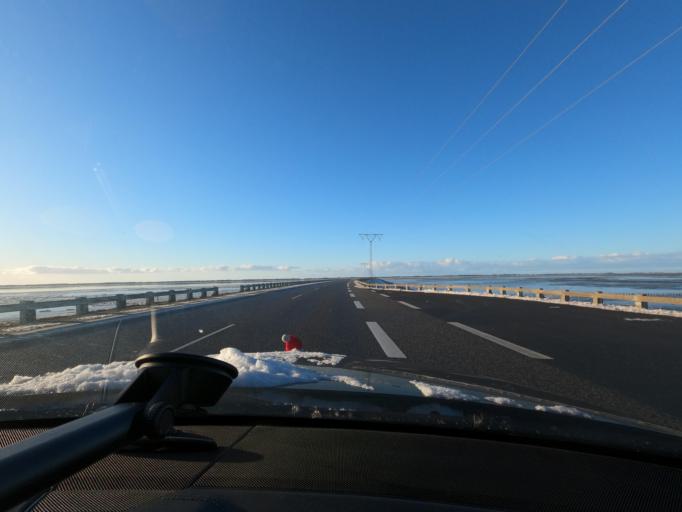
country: DK
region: South Denmark
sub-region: Tonder Kommune
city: Sherrebek
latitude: 55.1466
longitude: 8.6111
